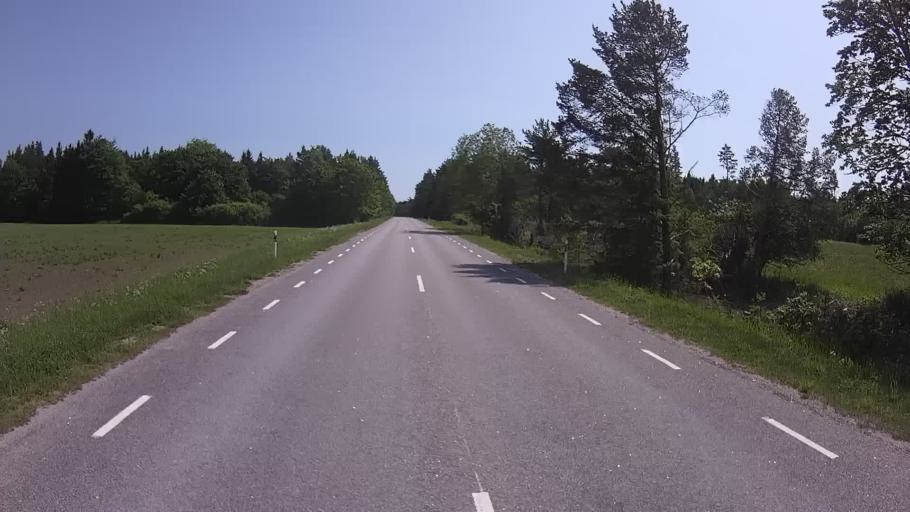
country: EE
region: Saare
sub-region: Kuressaare linn
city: Kuressaare
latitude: 58.3583
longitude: 22.0648
